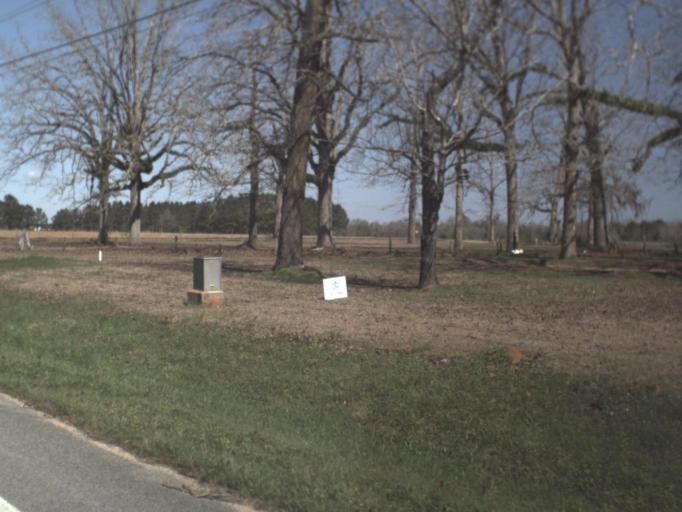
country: US
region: Florida
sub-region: Gadsden County
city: Quincy
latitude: 30.6474
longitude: -84.6008
